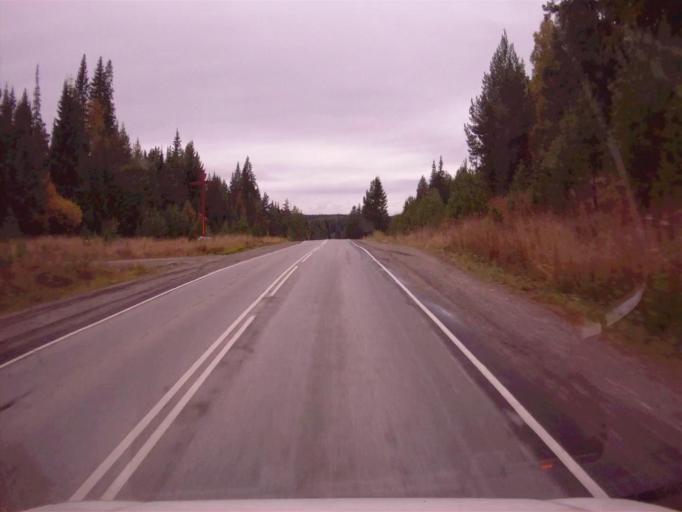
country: RU
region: Chelyabinsk
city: Nyazepetrovsk
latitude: 56.0662
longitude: 59.6692
